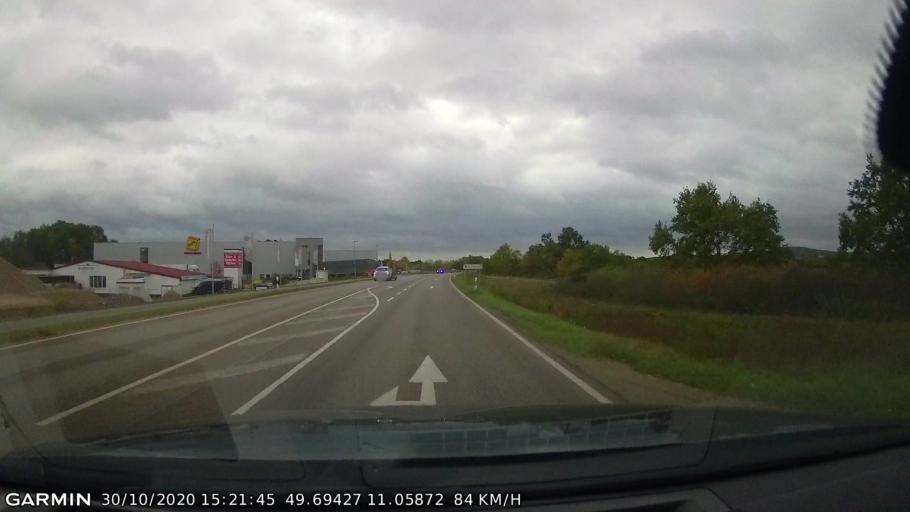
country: DE
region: Bavaria
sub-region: Upper Franconia
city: Forchheim
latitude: 49.6942
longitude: 11.0586
